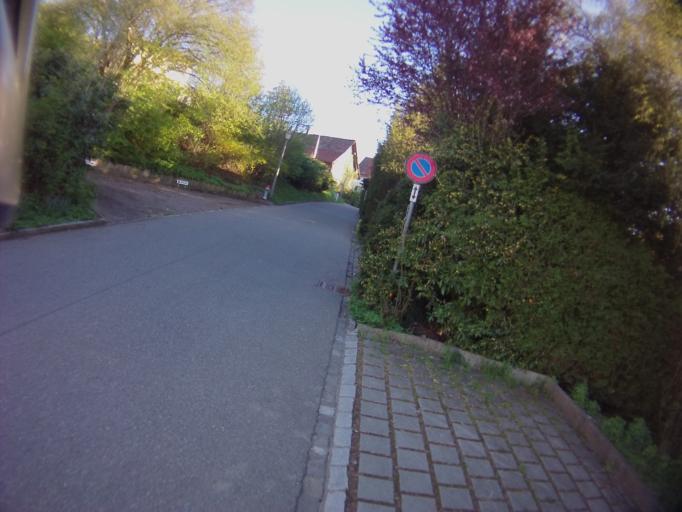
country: CH
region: Zurich
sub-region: Bezirk Dietikon
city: Birmensdorf
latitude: 47.3527
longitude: 8.4416
